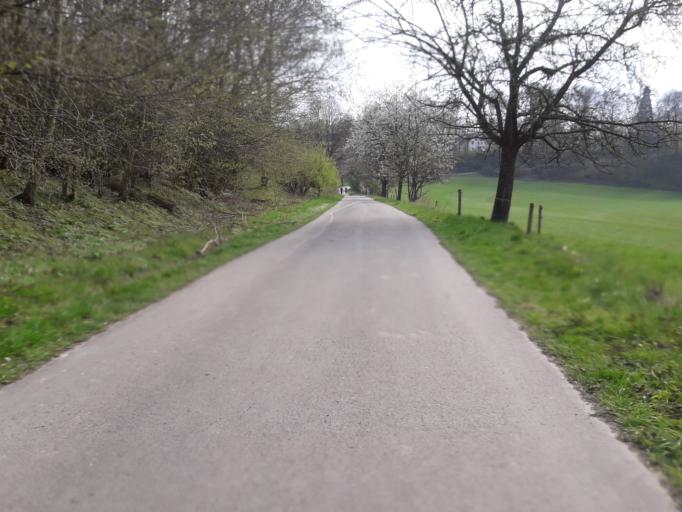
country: DE
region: North Rhine-Westphalia
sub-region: Regierungsbezirk Detmold
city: Paderborn
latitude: 51.6676
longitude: 8.7766
